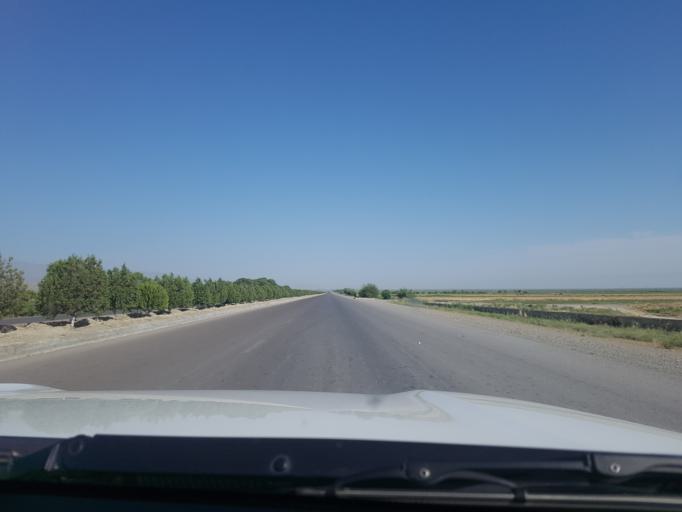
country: TM
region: Ahal
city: Baharly
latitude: 38.3373
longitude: 57.5695
